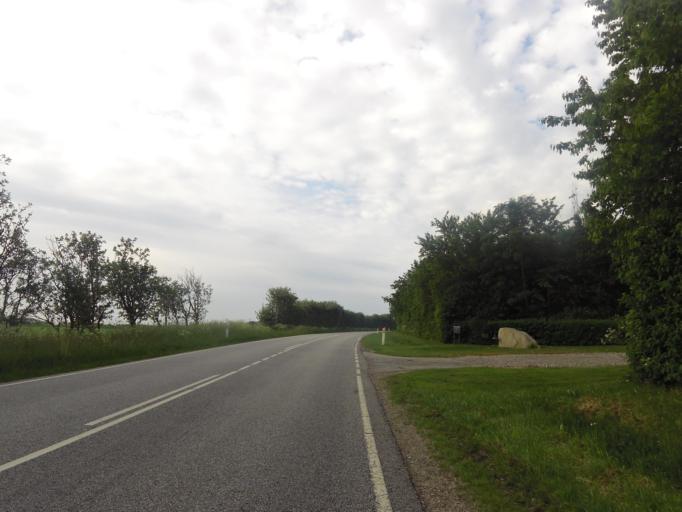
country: DK
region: South Denmark
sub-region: Haderslev Kommune
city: Gram
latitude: 55.2380
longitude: 8.9651
